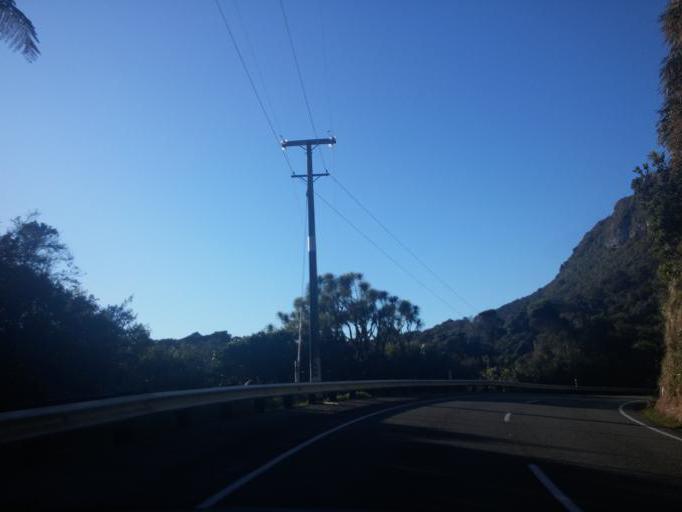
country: NZ
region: West Coast
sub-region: Grey District
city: Greymouth
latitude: -42.1014
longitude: 171.3403
